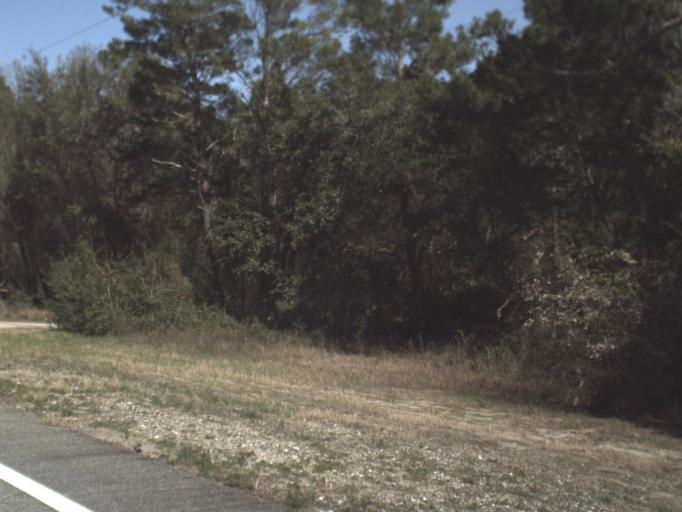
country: US
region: Florida
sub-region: Wakulla County
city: Crawfordville
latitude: 29.9283
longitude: -84.3993
